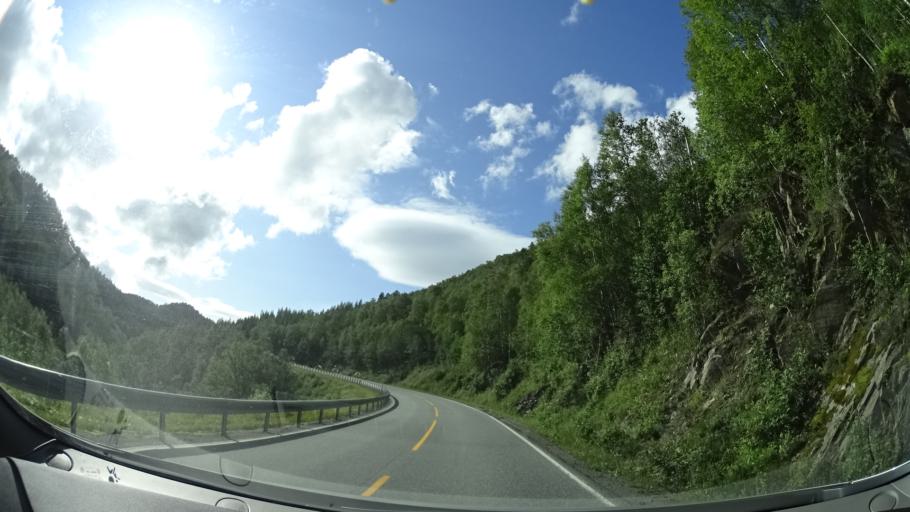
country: NO
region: Sor-Trondelag
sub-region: Hemne
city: Kyrksaeterora
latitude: 63.2126
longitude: 9.1422
